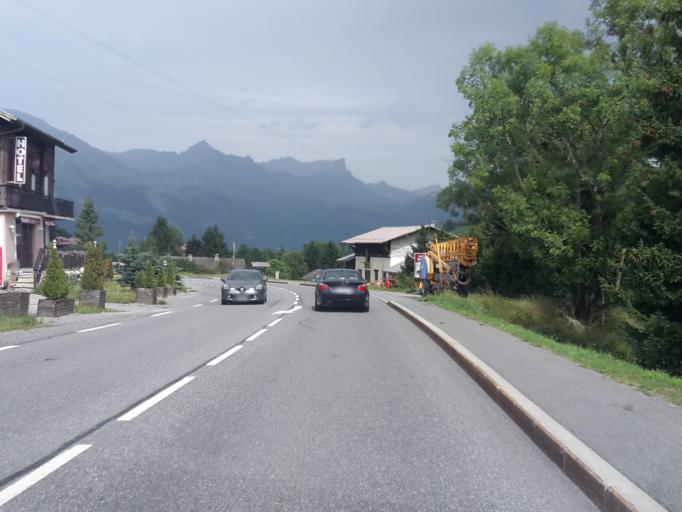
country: FR
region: Rhone-Alpes
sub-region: Departement de la Haute-Savoie
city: Combloux
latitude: 45.8777
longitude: 6.6366
